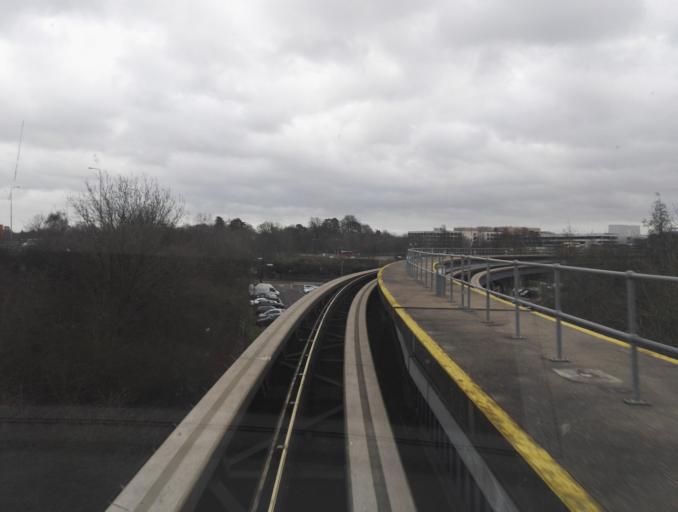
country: GB
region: England
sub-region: Surrey
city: Horley
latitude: 51.1596
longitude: -0.1634
